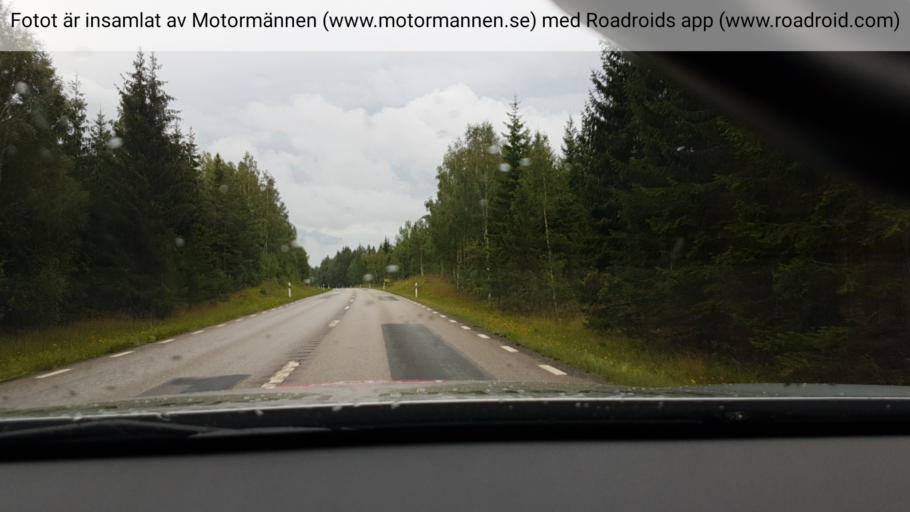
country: SE
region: Uppsala
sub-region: Alvkarleby Kommun
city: AElvkarleby
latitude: 60.5576
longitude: 17.4675
